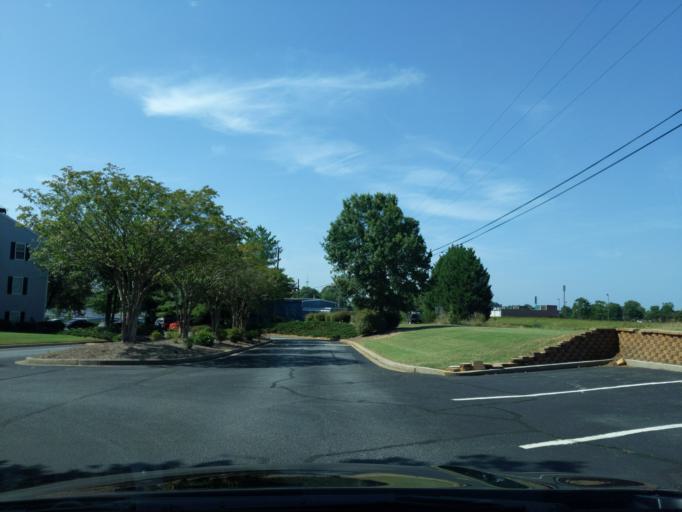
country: US
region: South Carolina
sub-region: Spartanburg County
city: Saxon
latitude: 34.9855
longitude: -81.9668
